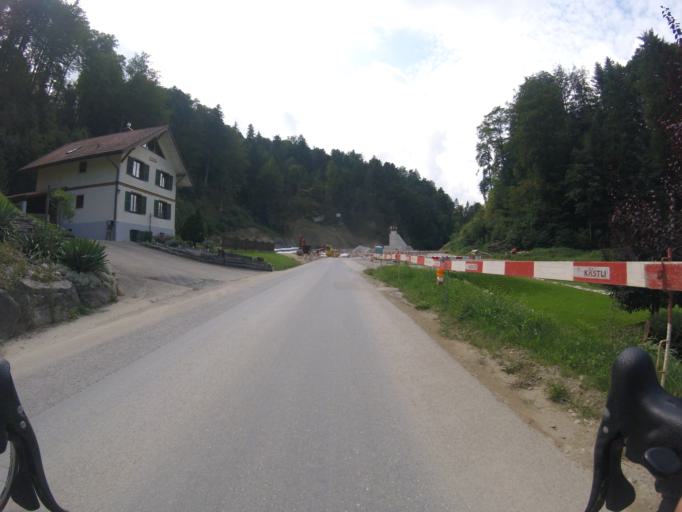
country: CH
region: Bern
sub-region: Emmental District
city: Oberburg
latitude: 47.0309
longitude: 7.6092
